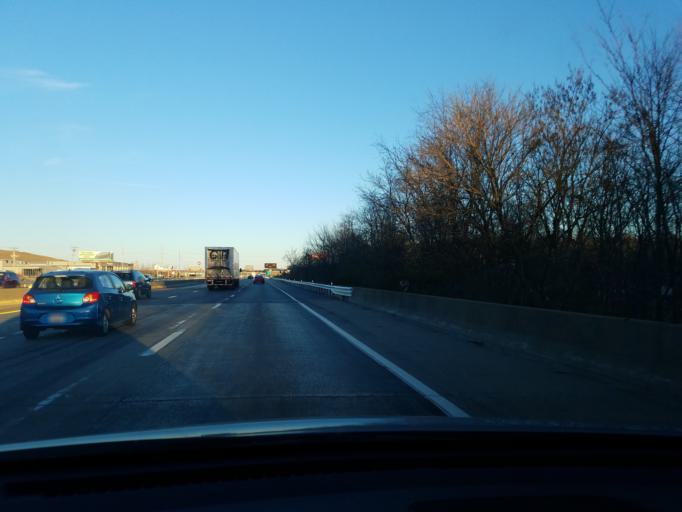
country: US
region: Missouri
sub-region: Saint Louis County
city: Valley Park
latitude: 38.5362
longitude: -90.5130
